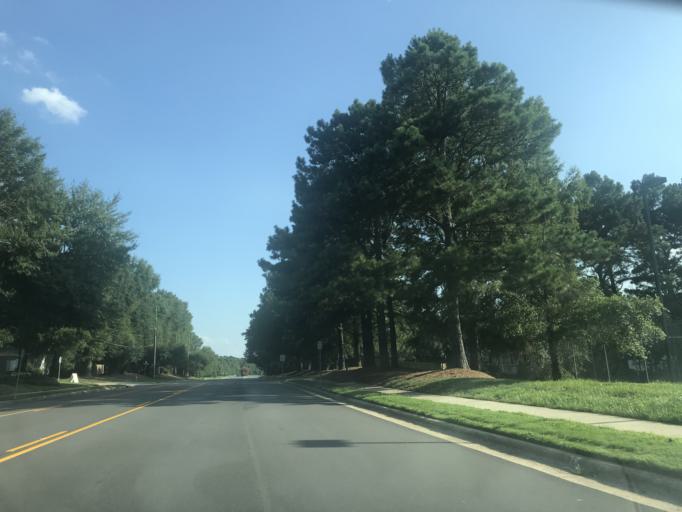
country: US
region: North Carolina
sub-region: Wake County
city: Knightdale
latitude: 35.7830
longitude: -78.5454
